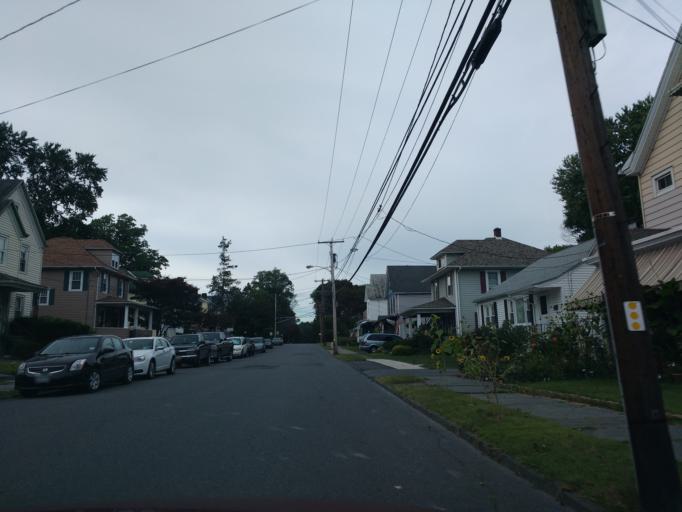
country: US
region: New York
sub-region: Ulster County
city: Kingston
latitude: 41.9248
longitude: -73.9999
